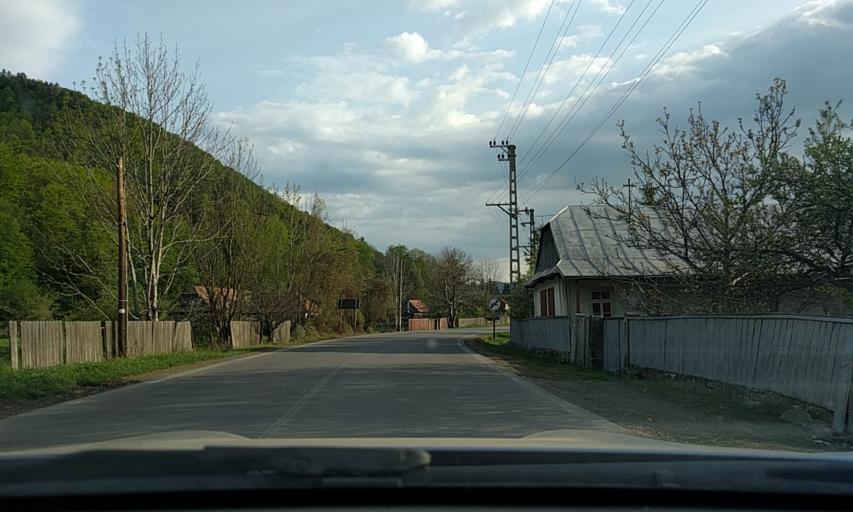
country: RO
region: Bacau
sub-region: Oras Slanic-Moldova
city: Slanic-Moldova
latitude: 46.1371
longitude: 26.4504
